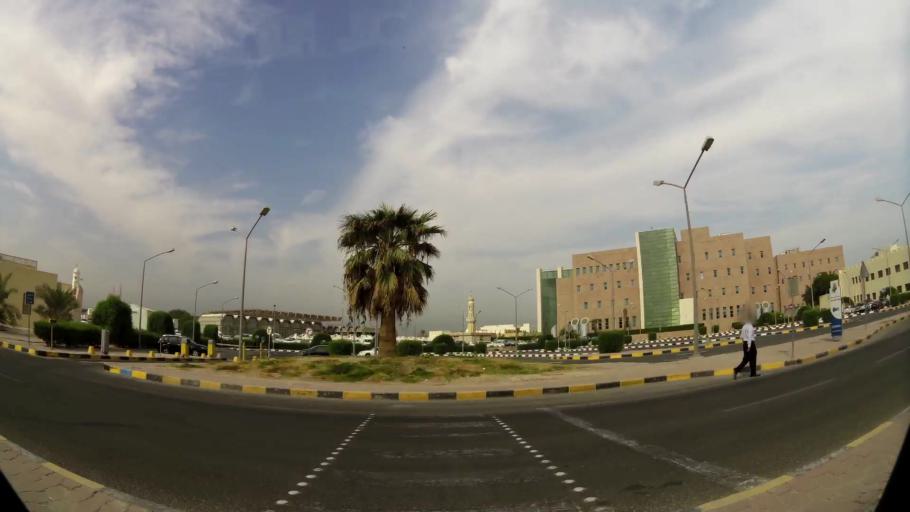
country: KW
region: Al Asimah
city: Kuwait City
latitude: 29.3739
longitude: 47.9700
